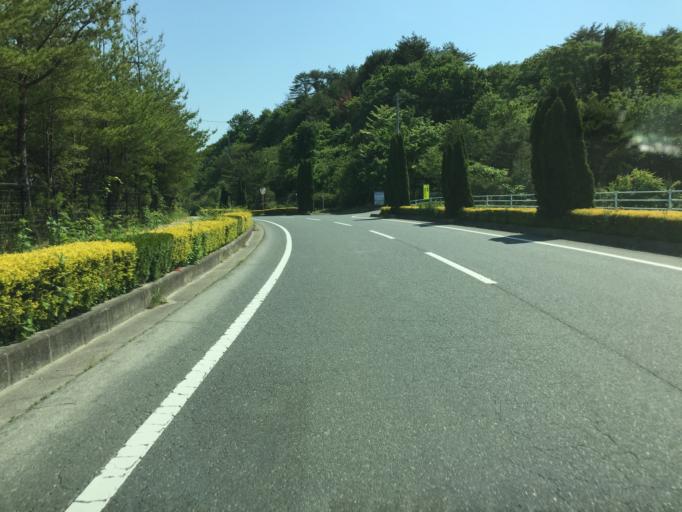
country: JP
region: Miyagi
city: Marumori
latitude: 37.8373
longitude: 140.8813
